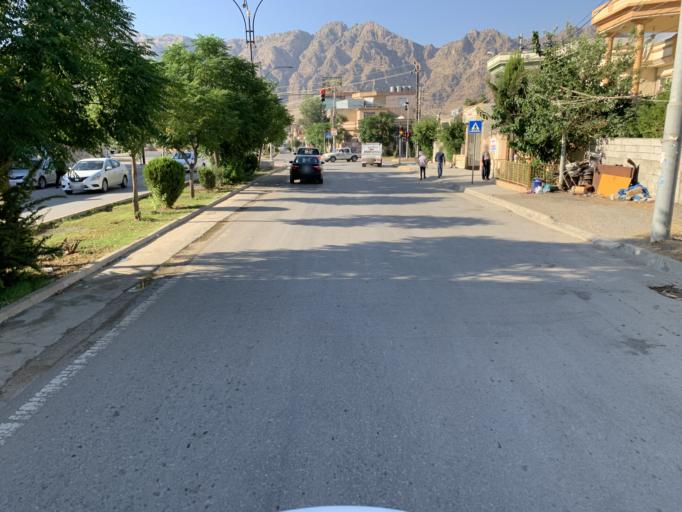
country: IQ
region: As Sulaymaniyah
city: Raniye
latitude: 36.2505
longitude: 44.8767
